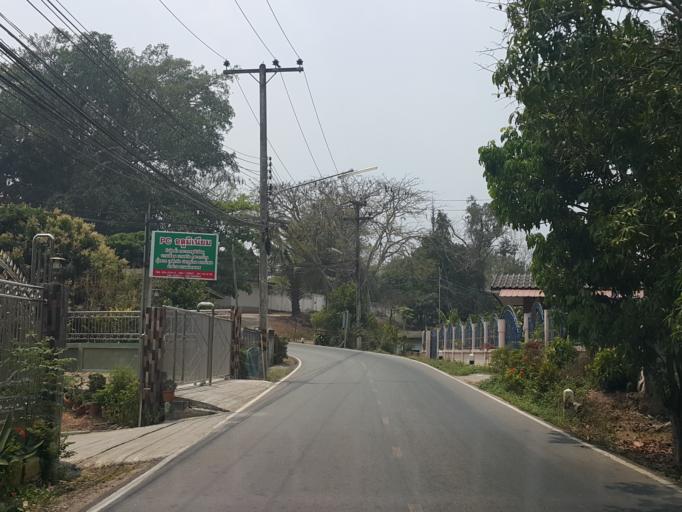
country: TH
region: Chiang Mai
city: Mae Taeng
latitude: 19.0250
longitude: 98.8749
